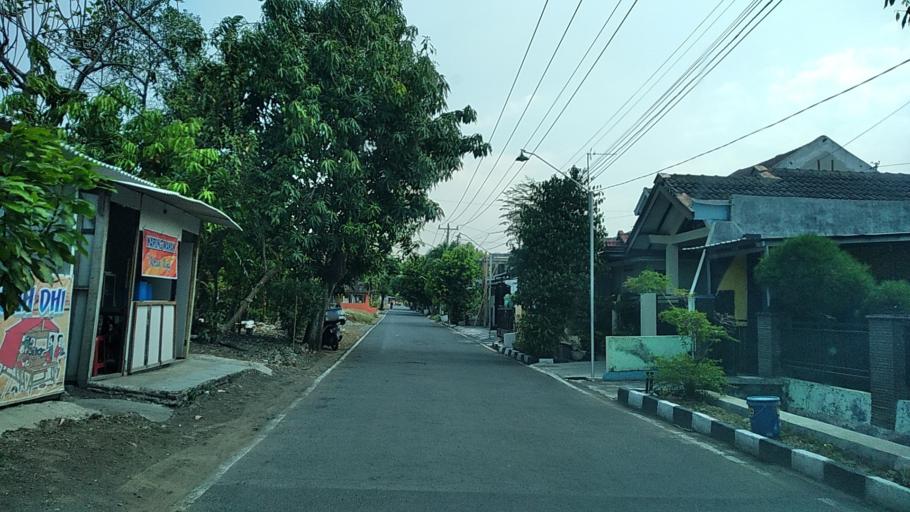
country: ID
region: Central Java
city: Mranggen
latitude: -7.0468
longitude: 110.4811
